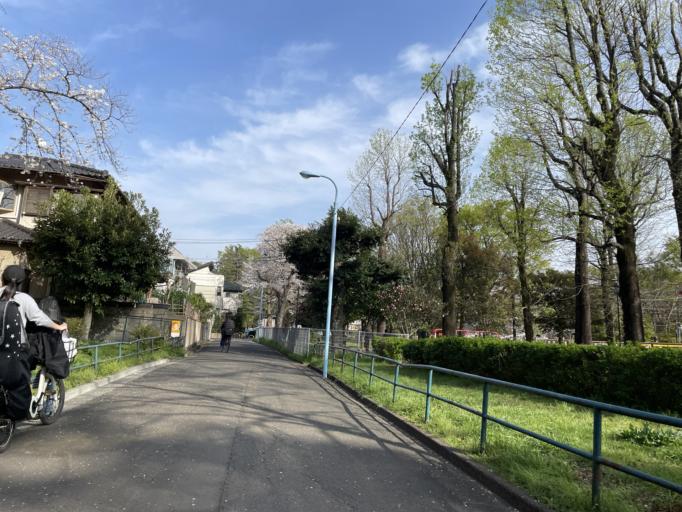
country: JP
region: Tokyo
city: Tokyo
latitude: 35.6866
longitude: 139.6355
